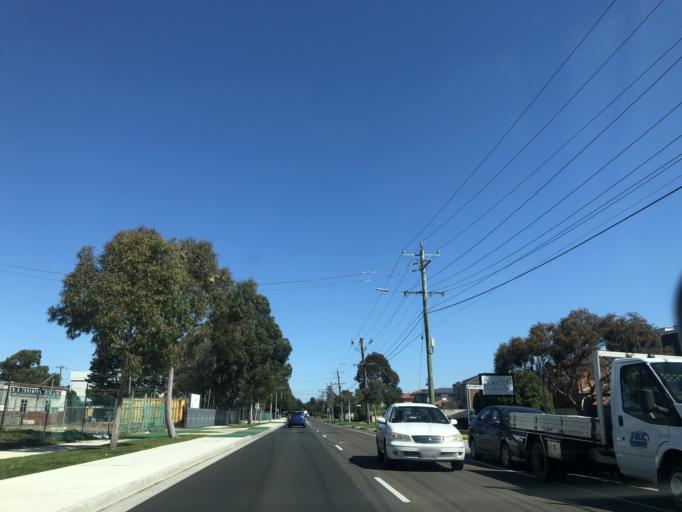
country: AU
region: Victoria
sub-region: Monash
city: Clayton
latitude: -37.9039
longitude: 145.1285
